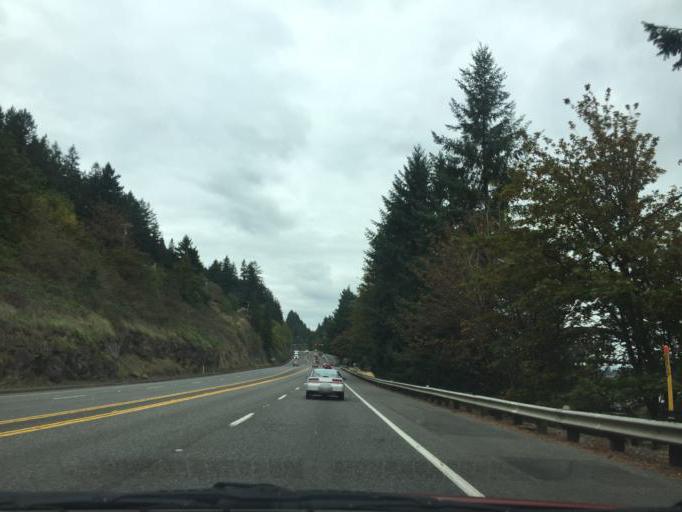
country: US
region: Oregon
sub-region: Washington County
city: Bethany
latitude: 45.6237
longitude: -122.8143
